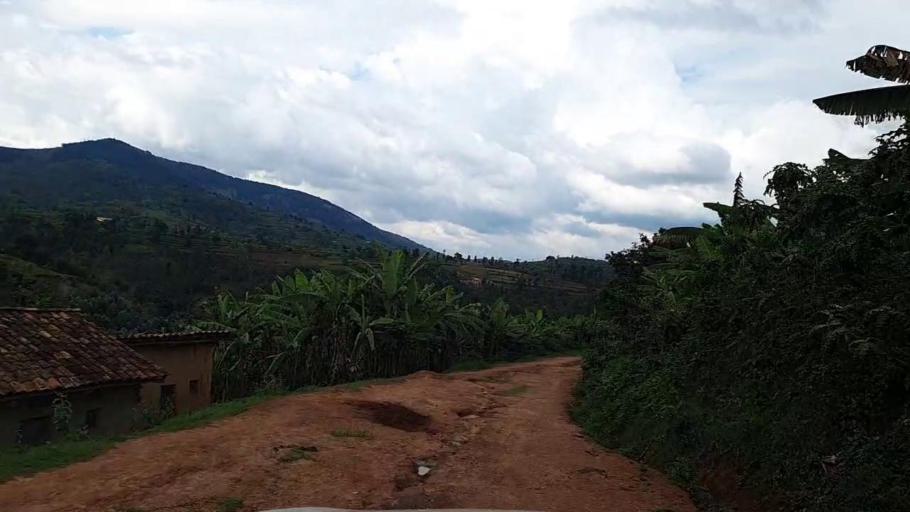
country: RW
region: Southern Province
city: Gikongoro
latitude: -2.4179
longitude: 29.6546
